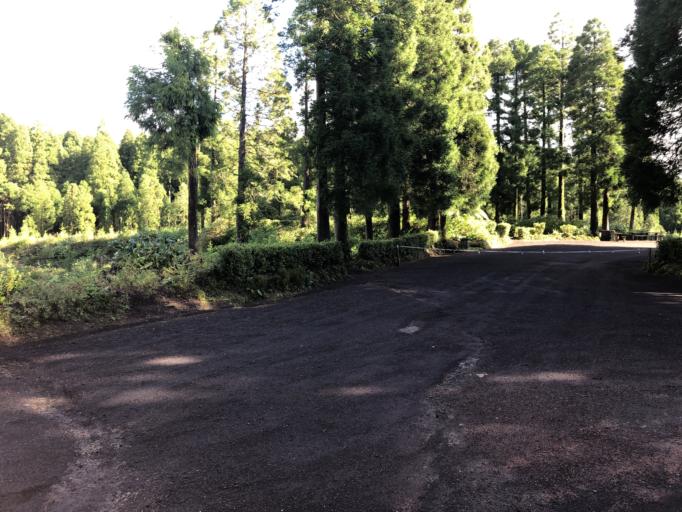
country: PT
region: Azores
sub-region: Ponta Delgada
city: Arrifes
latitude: 37.8383
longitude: -25.7589
